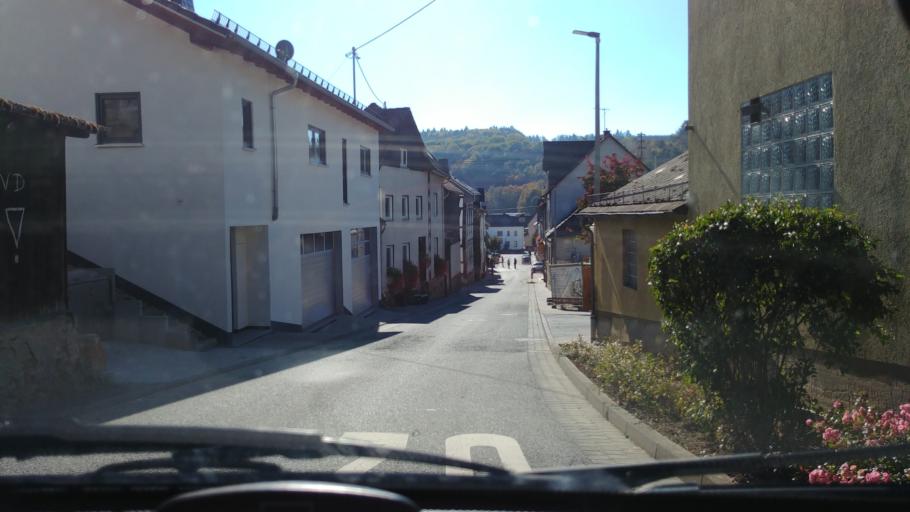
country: DE
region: Rheinland-Pfalz
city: Burgschwalbach
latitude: 50.2296
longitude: 8.1208
